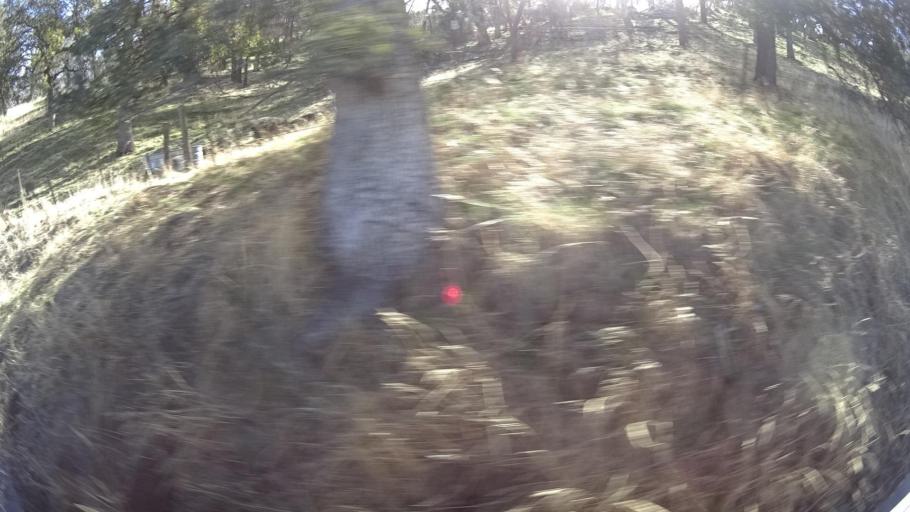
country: US
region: California
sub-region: Kern County
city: Alta Sierra
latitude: 35.6334
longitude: -118.7625
